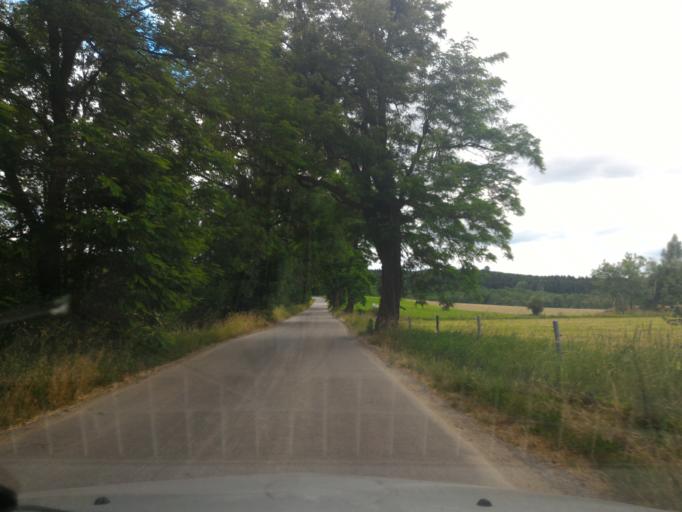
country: CZ
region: Vysocina
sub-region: Okres Jihlava
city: Telc
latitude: 49.2243
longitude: 15.3869
